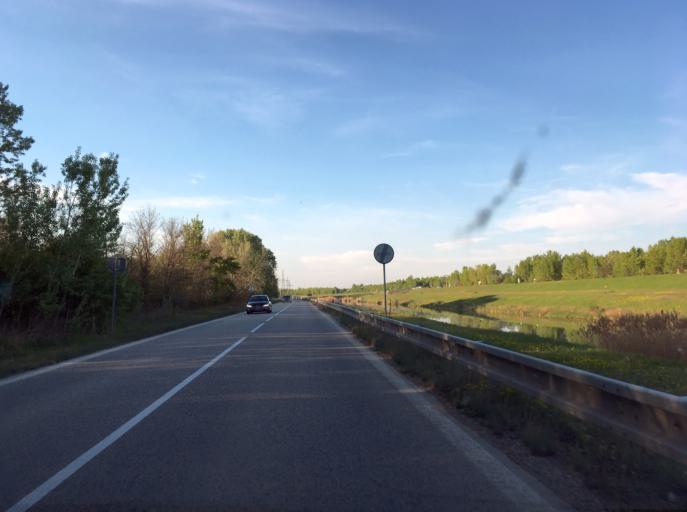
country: HU
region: Gyor-Moson-Sopron
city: Rajka
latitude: 48.0231
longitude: 17.2046
